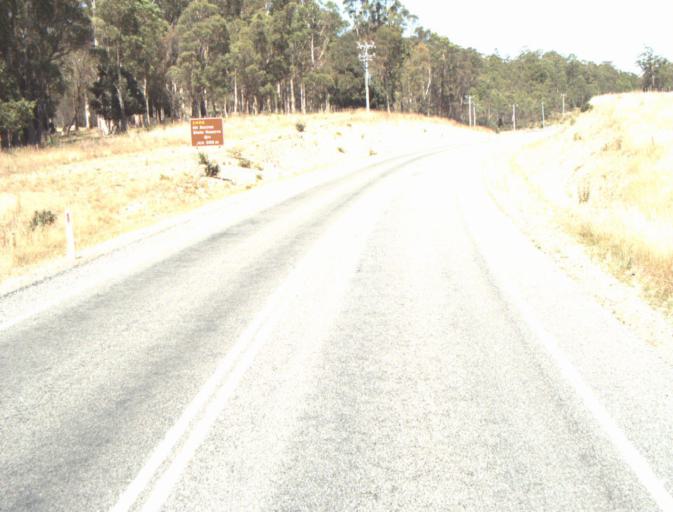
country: AU
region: Tasmania
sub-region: Launceston
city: Newstead
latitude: -41.3392
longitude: 147.3472
